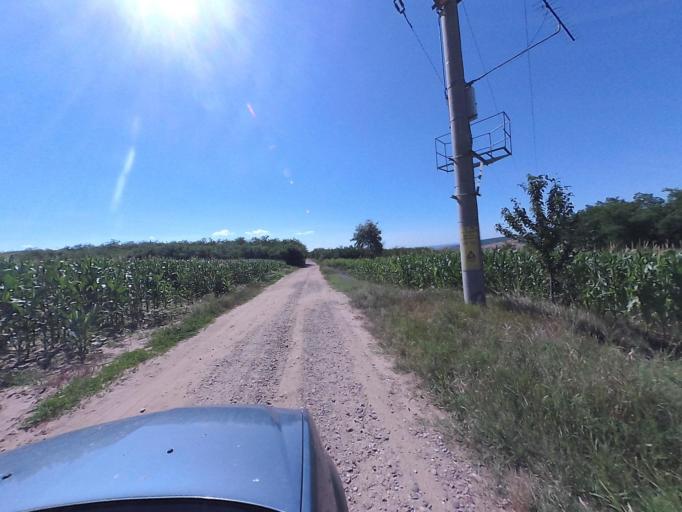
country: RO
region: Vaslui
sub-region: Comuna Costesti
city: Costesti
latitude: 46.4852
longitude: 27.7705
